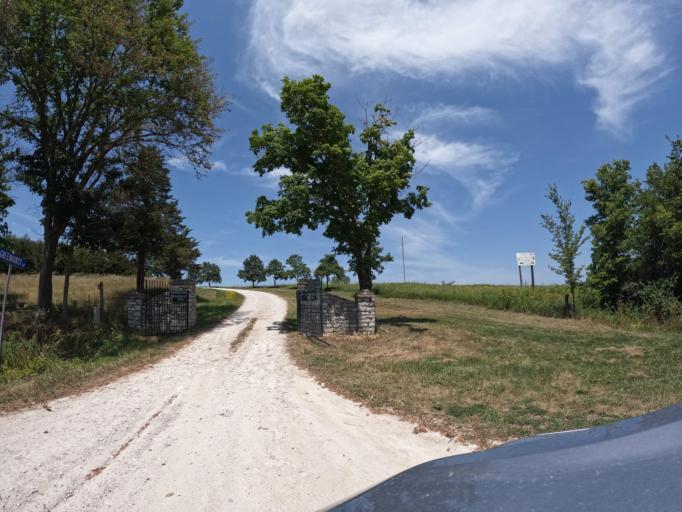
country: US
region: Iowa
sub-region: Henry County
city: Mount Pleasant
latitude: 40.9390
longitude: -91.5815
